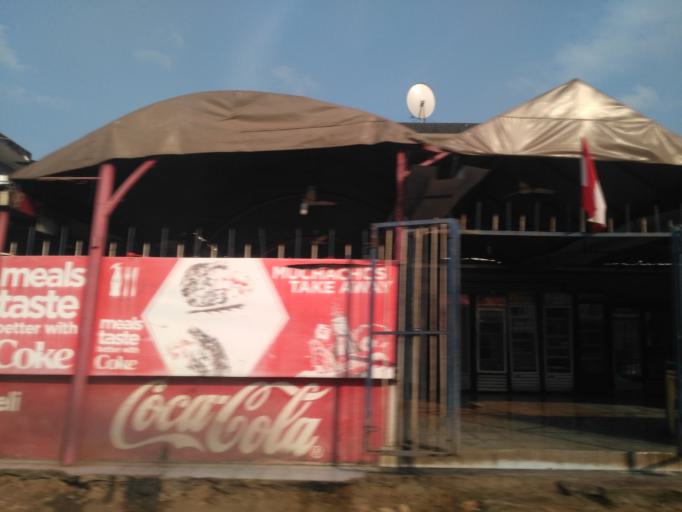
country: TZ
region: Dar es Salaam
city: Dar es Salaam
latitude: -6.8103
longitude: 39.2783
